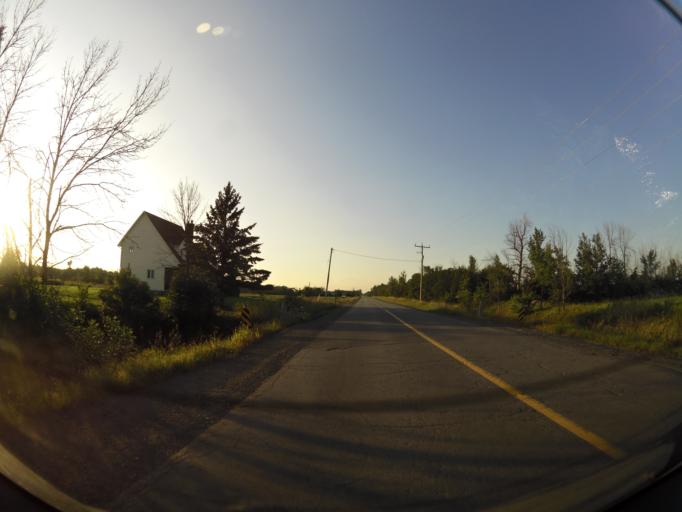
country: CA
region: Ontario
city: Clarence-Rockland
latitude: 45.4767
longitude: -75.4388
